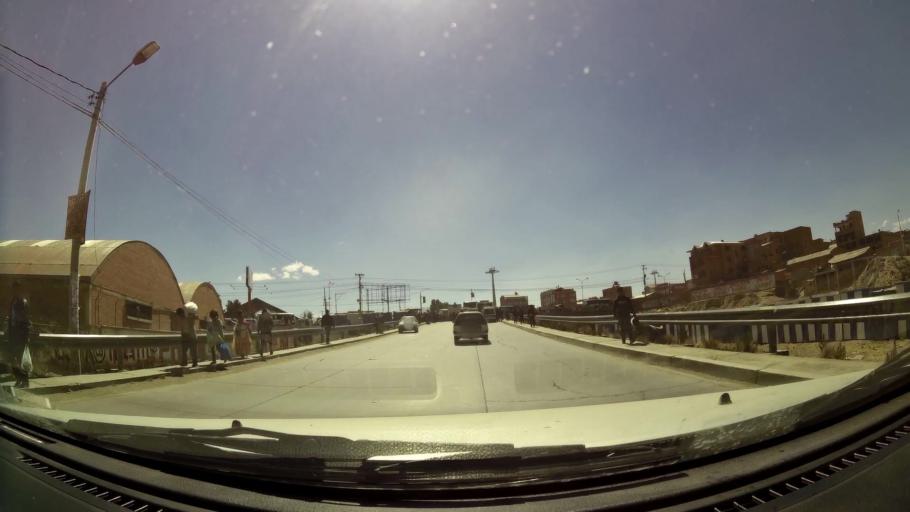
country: BO
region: La Paz
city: La Paz
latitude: -16.4918
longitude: -68.2030
